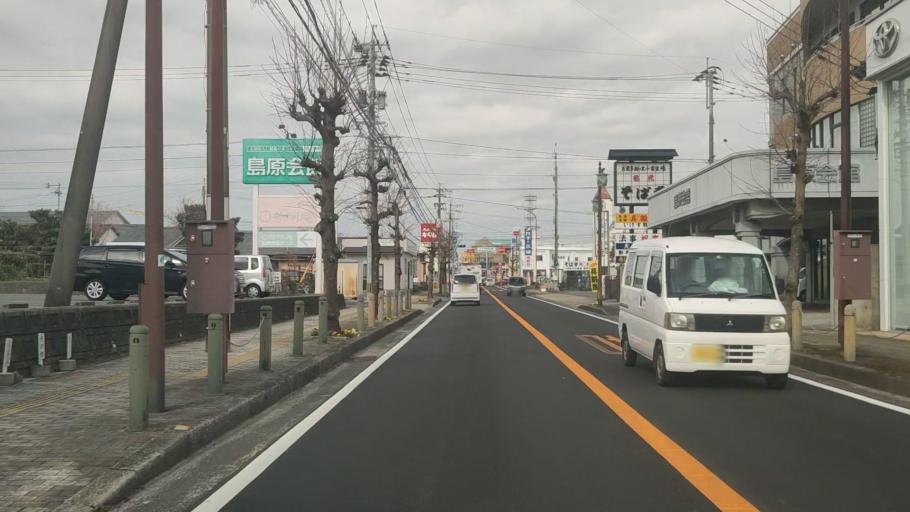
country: JP
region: Nagasaki
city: Shimabara
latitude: 32.7944
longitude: 130.3684
